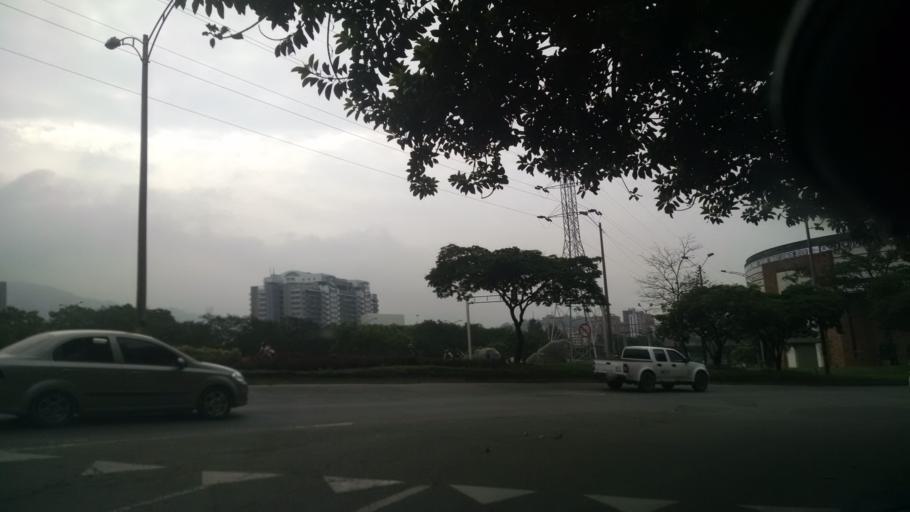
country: CO
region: Antioquia
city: Medellin
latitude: 6.2509
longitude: -75.5798
